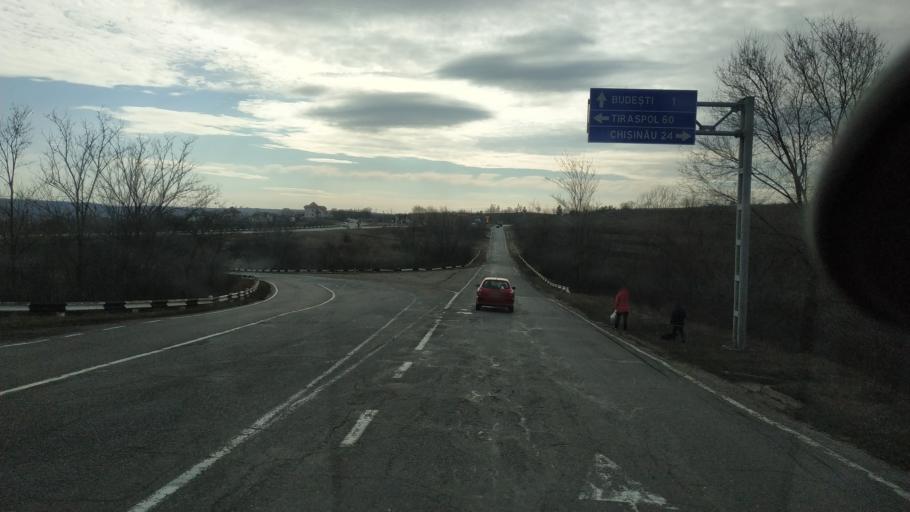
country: MD
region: Chisinau
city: Vadul lui Voda
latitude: 47.0733
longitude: 29.0210
